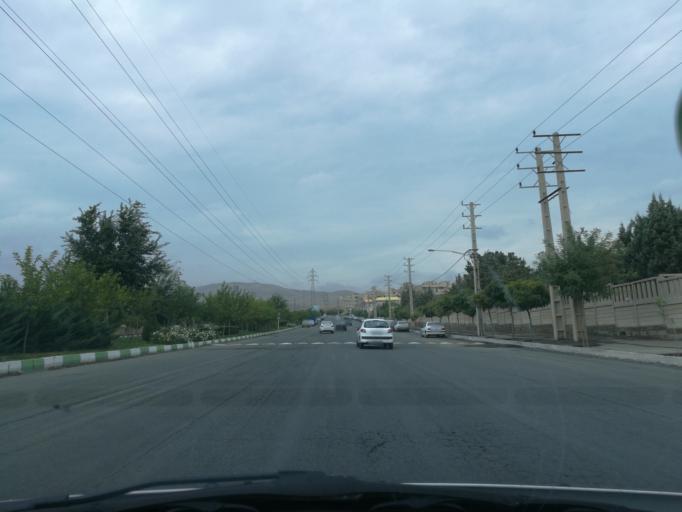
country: IR
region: Alborz
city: Karaj
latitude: 35.8600
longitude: 50.9242
